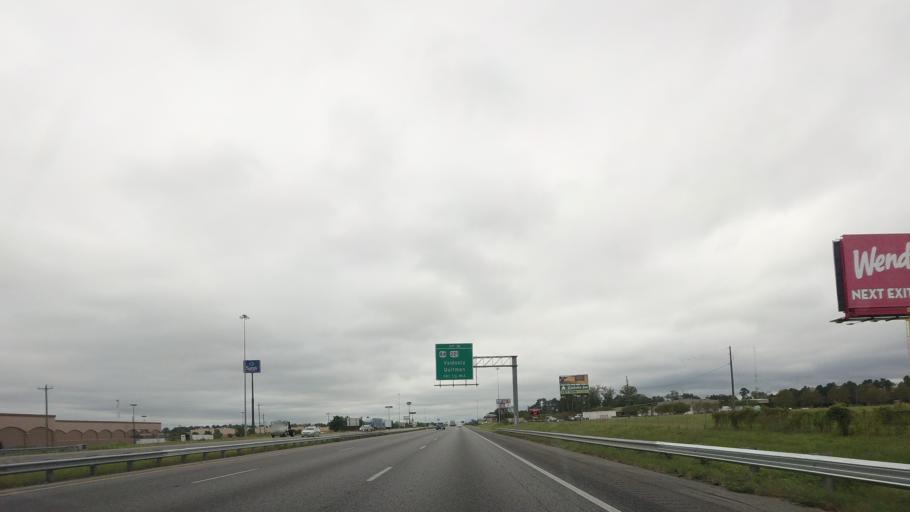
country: US
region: Georgia
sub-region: Lowndes County
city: Remerton
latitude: 30.8287
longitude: -83.3228
